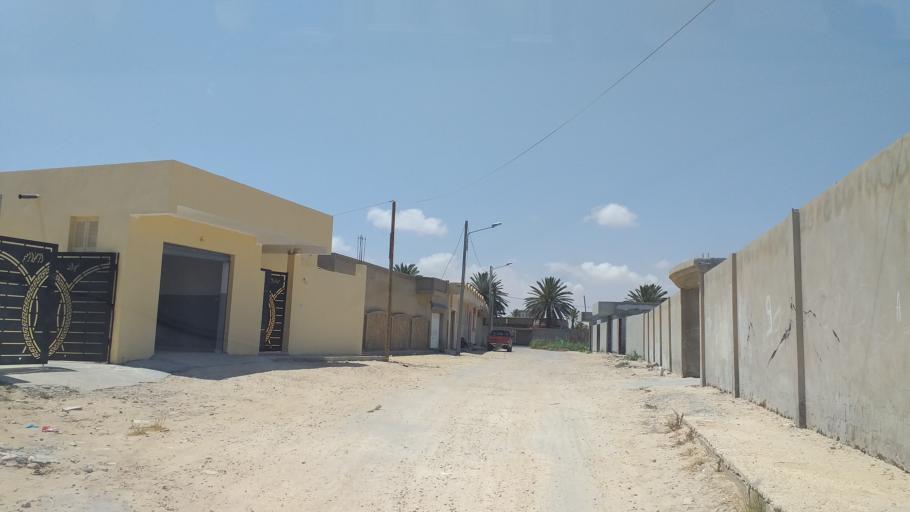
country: TN
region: Qabis
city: Gabes
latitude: 33.9447
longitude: 10.0564
